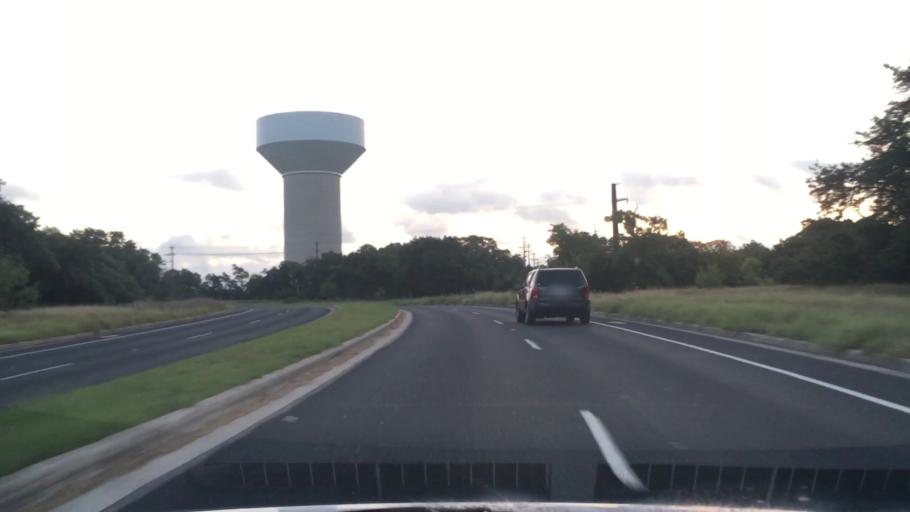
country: US
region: Texas
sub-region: Williamson County
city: Cedar Park
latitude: 30.4873
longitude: -97.8027
